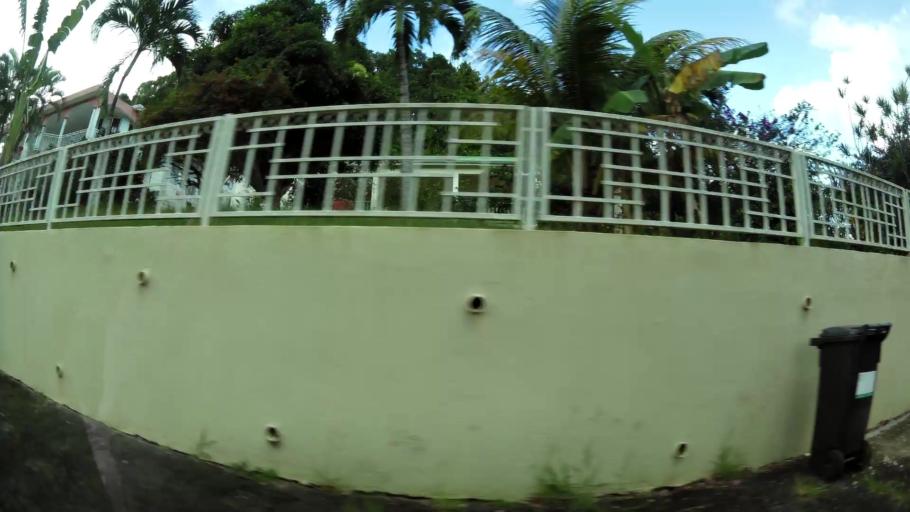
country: GP
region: Guadeloupe
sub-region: Guadeloupe
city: Pointe-a-Pitre
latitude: 16.2474
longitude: -61.5178
